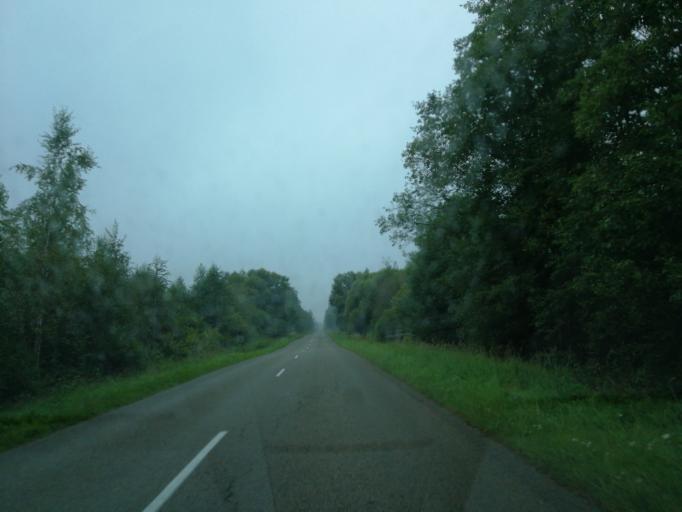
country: LV
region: Preilu Rajons
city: Jaunaglona
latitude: 56.2605
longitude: 26.9934
